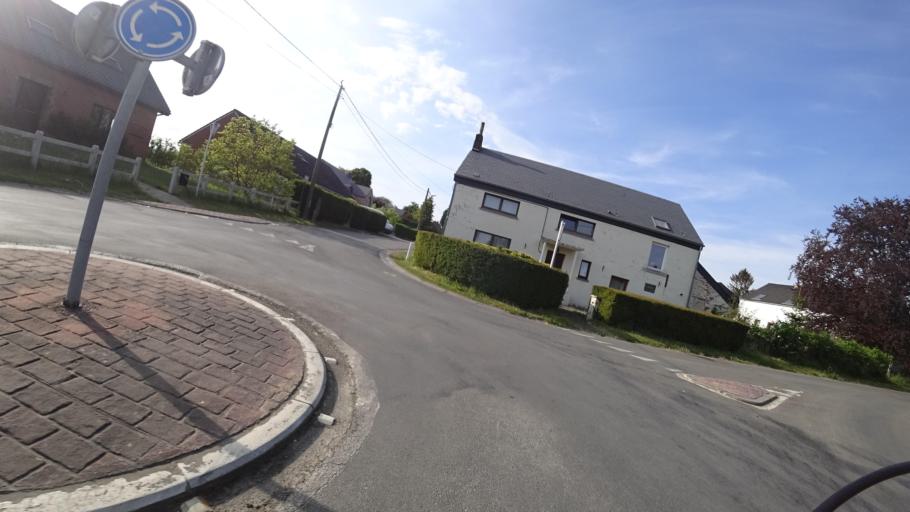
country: BE
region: Wallonia
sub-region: Province de Namur
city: Gembloux
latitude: 50.5296
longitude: 4.7839
